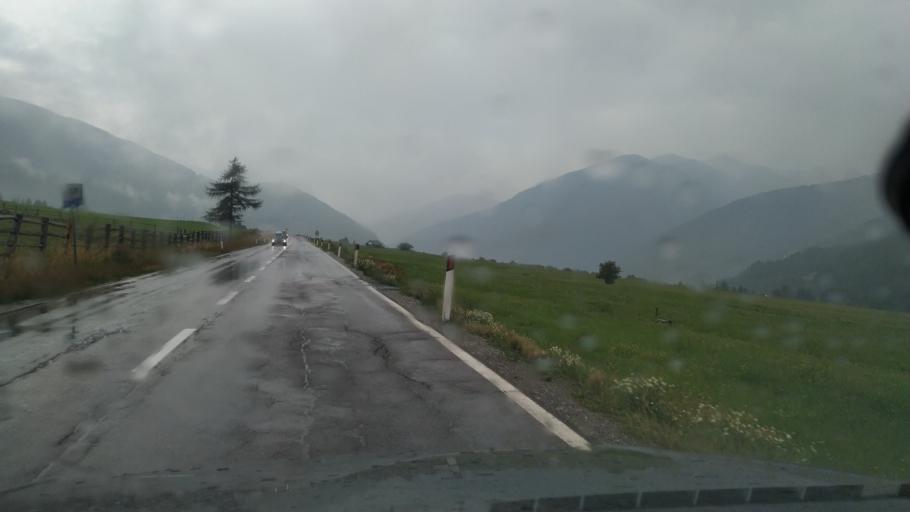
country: IT
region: Trentino-Alto Adige
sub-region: Bolzano
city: Malles Venosta
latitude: 46.7339
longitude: 10.5364
